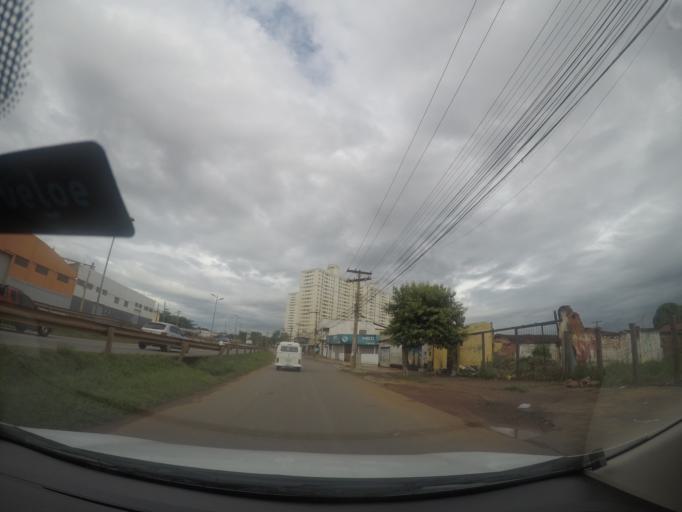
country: BR
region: Goias
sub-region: Goiania
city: Goiania
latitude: -16.6499
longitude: -49.3230
